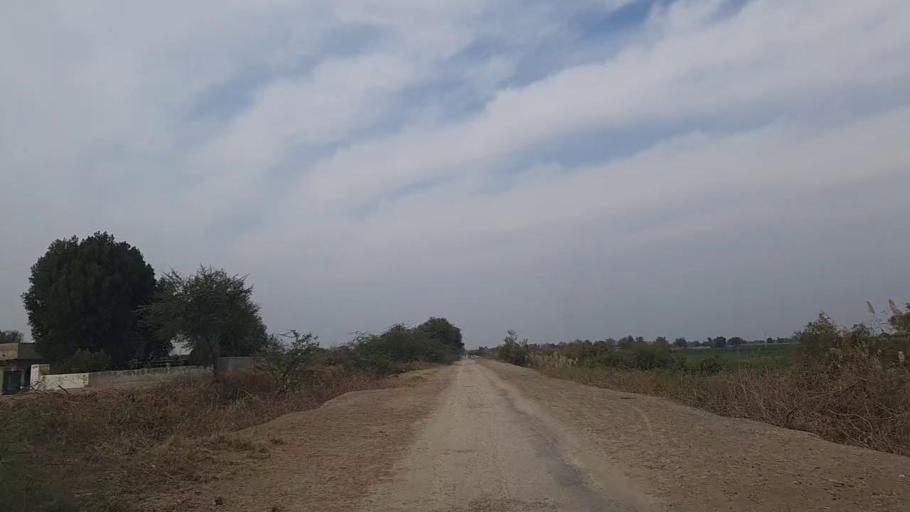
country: PK
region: Sindh
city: Daur
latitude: 26.4339
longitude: 68.4647
